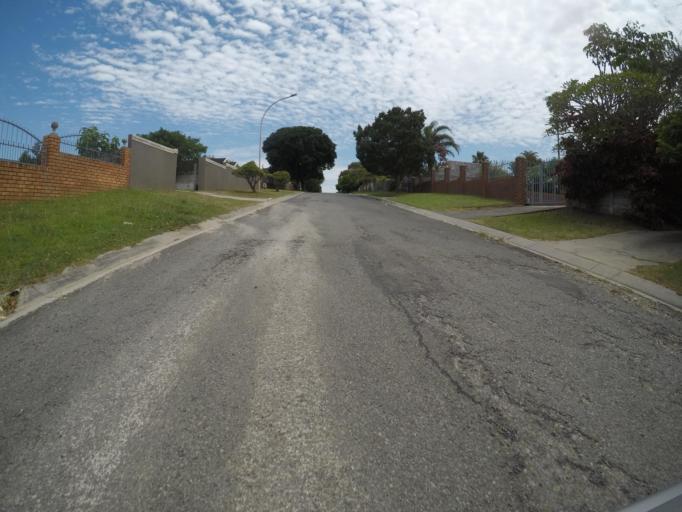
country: ZA
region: Eastern Cape
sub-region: Buffalo City Metropolitan Municipality
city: East London
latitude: -32.9822
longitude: 27.8649
